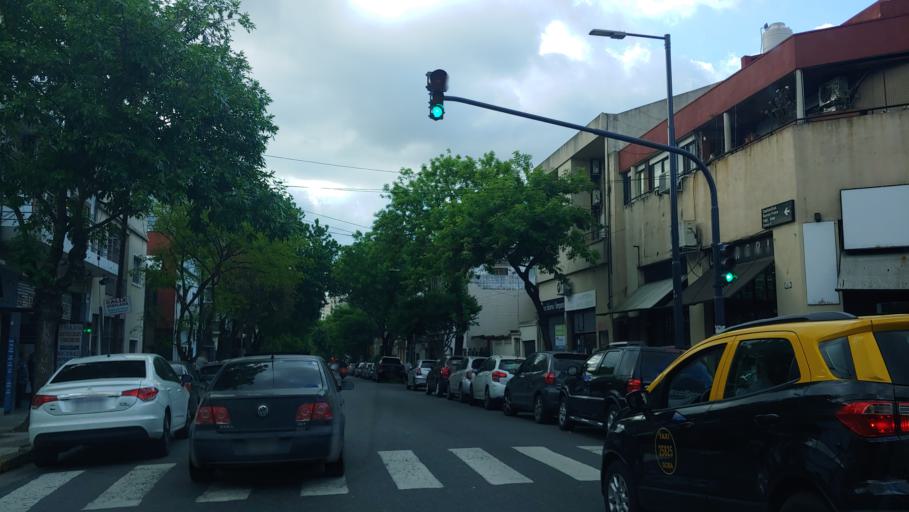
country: AR
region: Buenos Aires F.D.
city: Colegiales
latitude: -34.5753
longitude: -58.4527
